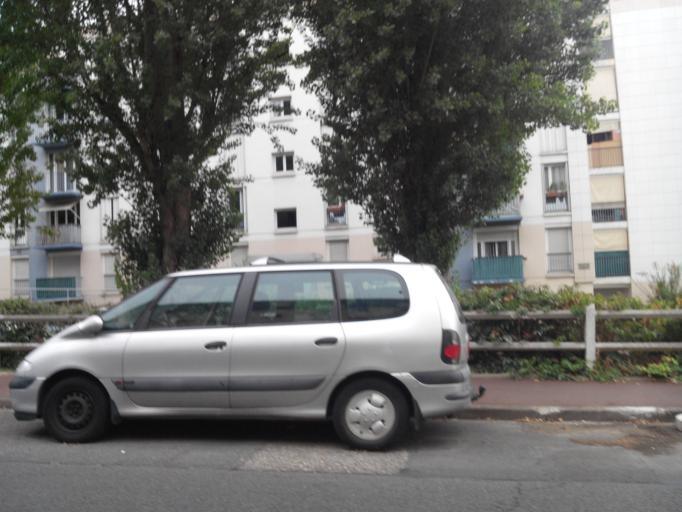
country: FR
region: Ile-de-France
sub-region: Departement du Val-de-Marne
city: L'Hay-les-Roses
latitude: 48.7875
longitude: 2.3326
